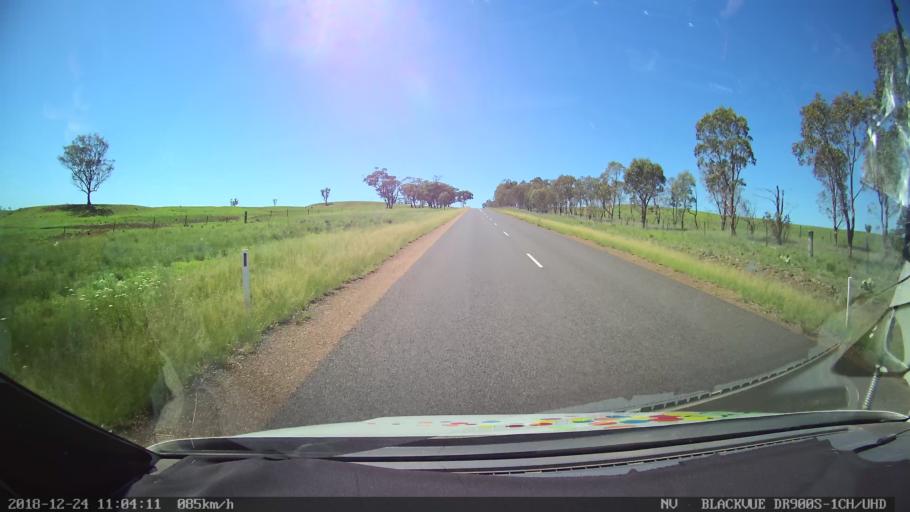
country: AU
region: New South Wales
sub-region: Upper Hunter Shire
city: Merriwa
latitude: -32.1059
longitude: 150.3708
